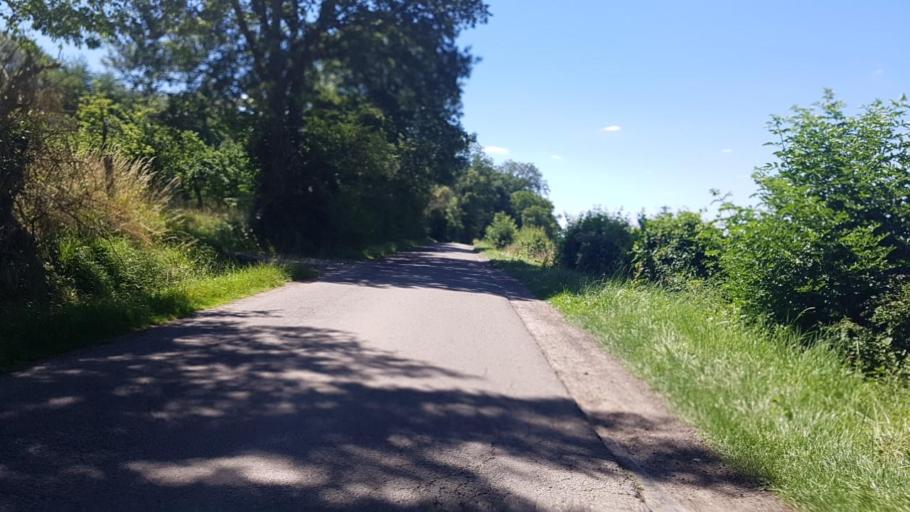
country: FR
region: Ile-de-France
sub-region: Departement de Seine-et-Marne
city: Fublaines
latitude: 48.9390
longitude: 2.9513
